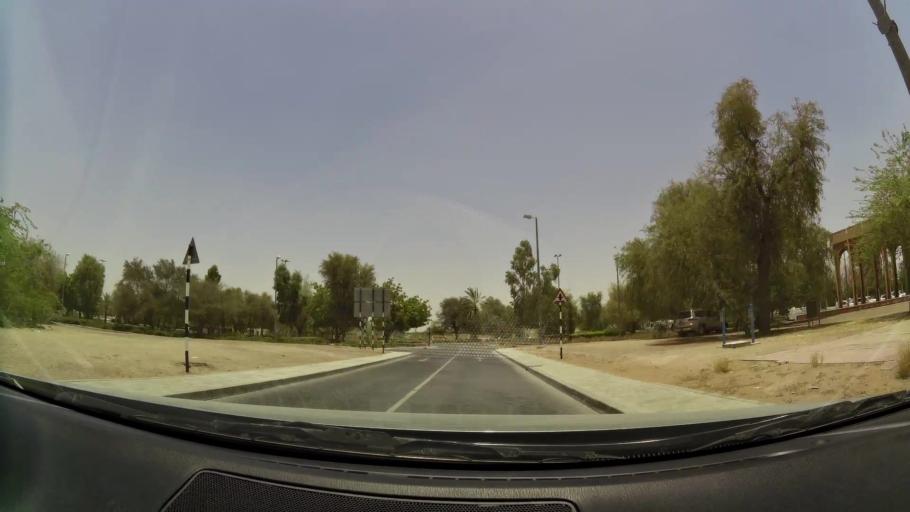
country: OM
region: Al Buraimi
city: Al Buraymi
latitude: 24.2635
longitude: 55.7395
